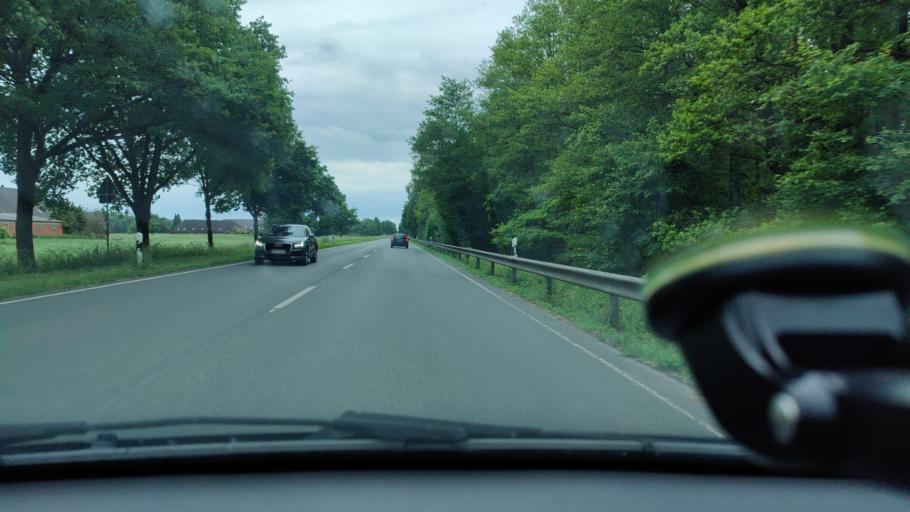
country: DE
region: North Rhine-Westphalia
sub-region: Regierungsbezirk Dusseldorf
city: Weeze
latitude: 51.6674
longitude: 6.2114
